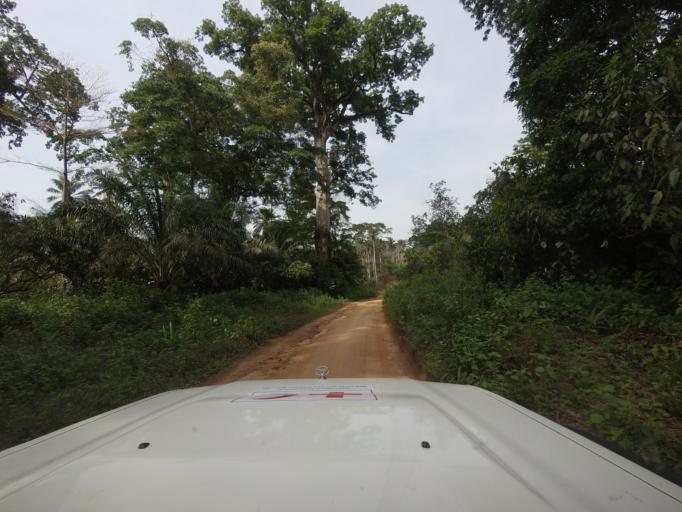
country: GN
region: Nzerekore
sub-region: Macenta
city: Macenta
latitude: 8.4631
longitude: -9.5790
